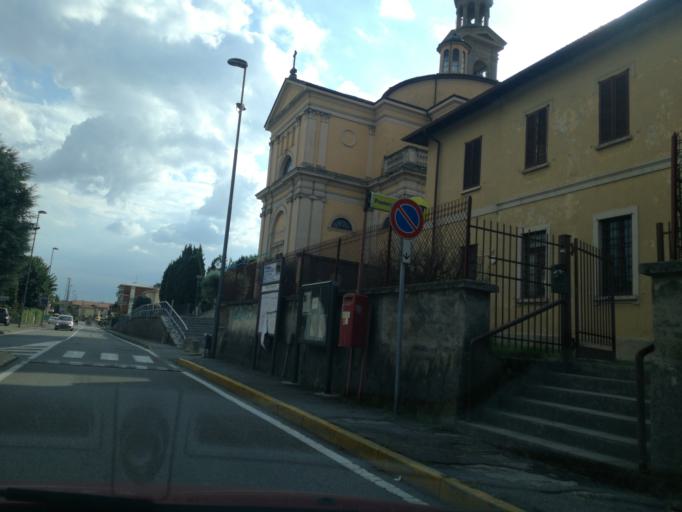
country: IT
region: Lombardy
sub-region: Provincia di Monza e Brianza
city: Villanova
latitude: 45.6256
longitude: 9.3856
